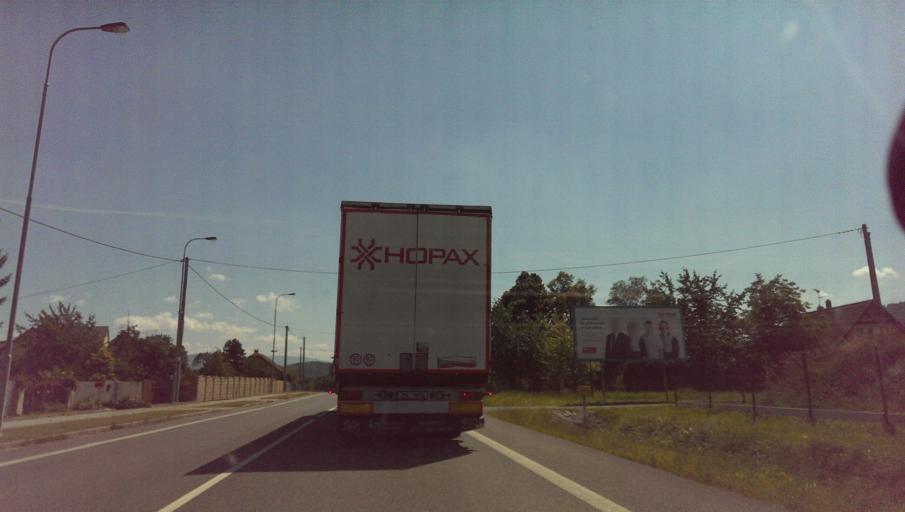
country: CZ
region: Moravskoslezsky
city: Koprivnice
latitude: 49.6100
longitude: 18.1653
